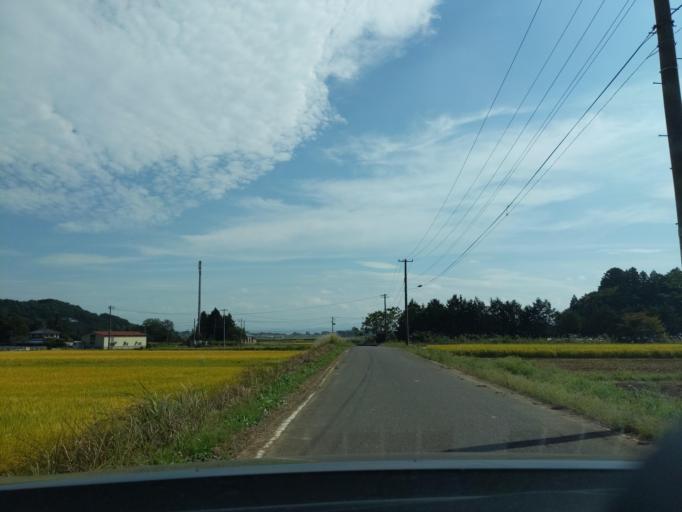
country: JP
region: Fukushima
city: Koriyama
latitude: 37.3689
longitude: 140.2703
